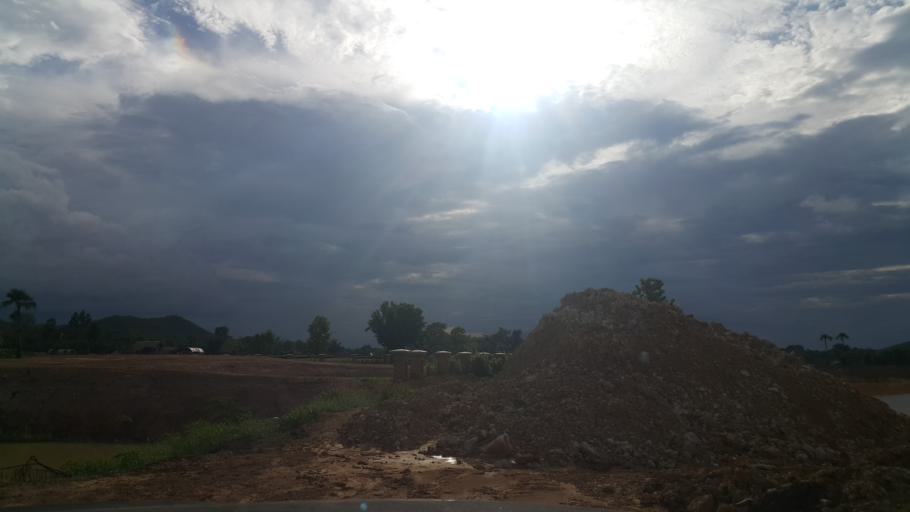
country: TH
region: Chiang Mai
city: Mae On
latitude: 18.7209
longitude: 99.2156
